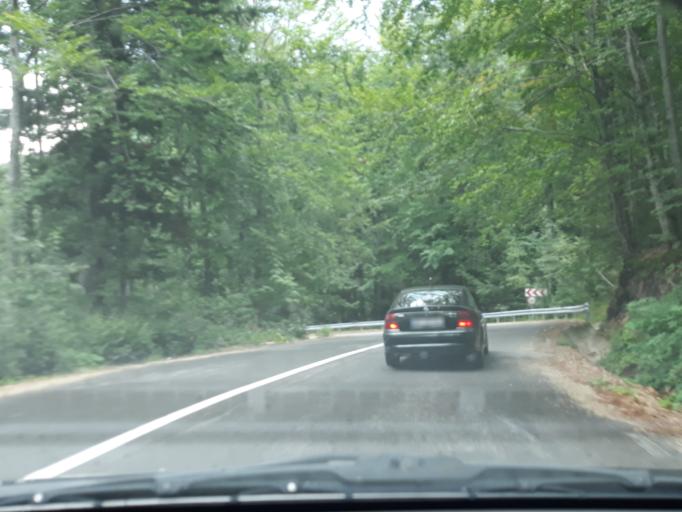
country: RO
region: Bihor
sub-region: Comuna Pietroasa
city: Pietroasa
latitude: 46.5980
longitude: 22.6688
